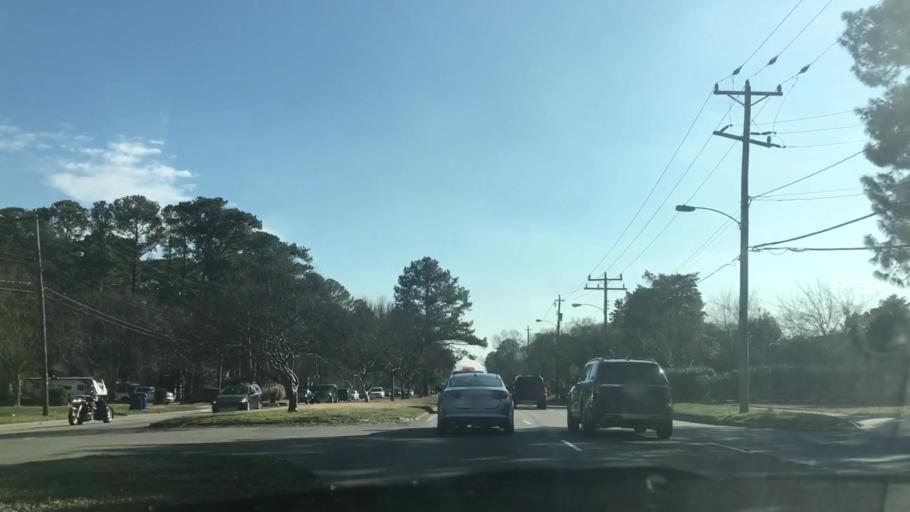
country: US
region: Virginia
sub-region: City of Norfolk
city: Norfolk
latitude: 36.8972
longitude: -76.2797
